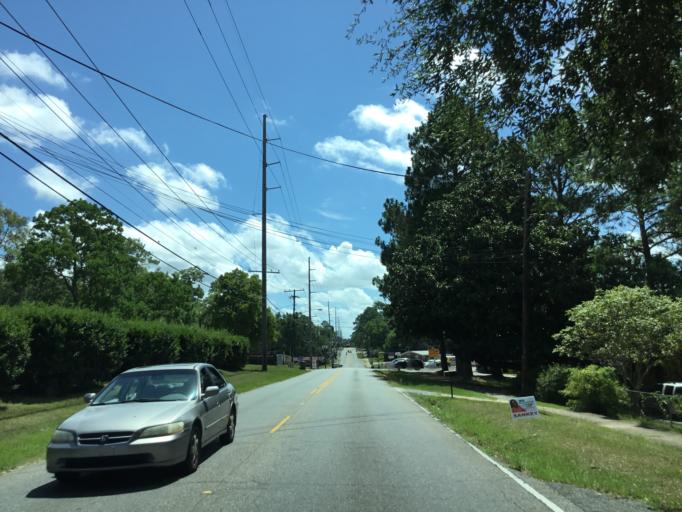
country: US
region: Alabama
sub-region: Montgomery County
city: Montgomery
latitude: 32.3670
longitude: -86.2580
